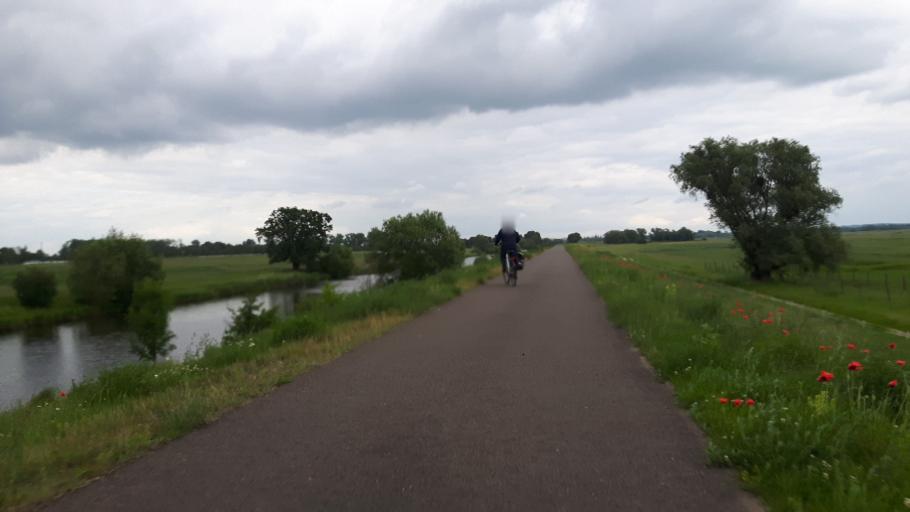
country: DE
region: Brandenburg
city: Meyenburg
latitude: 53.0279
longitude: 14.2495
